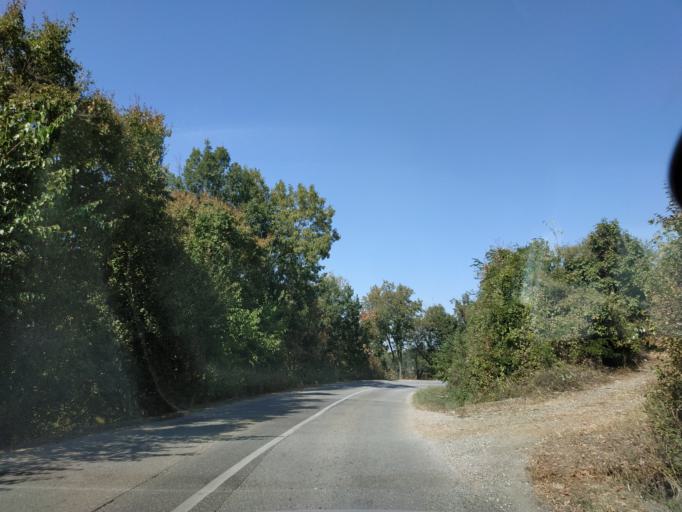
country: RS
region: Central Serbia
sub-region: Sumadijski Okrug
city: Topola
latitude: 44.2601
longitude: 20.6729
